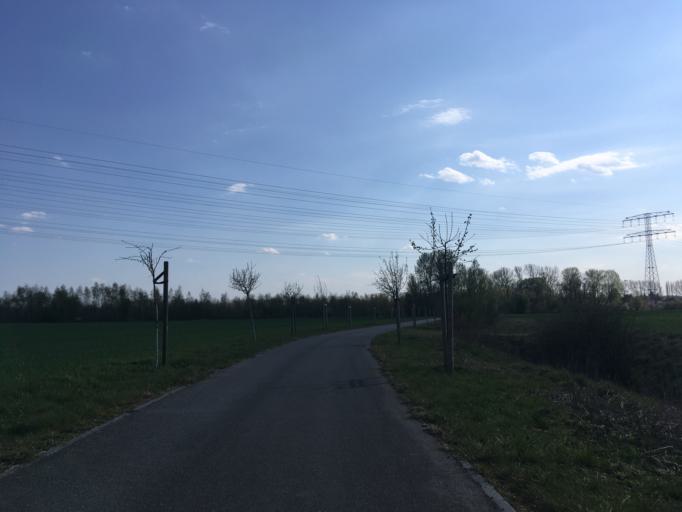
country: DE
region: Berlin
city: Wartenberg
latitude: 52.5915
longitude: 13.5005
